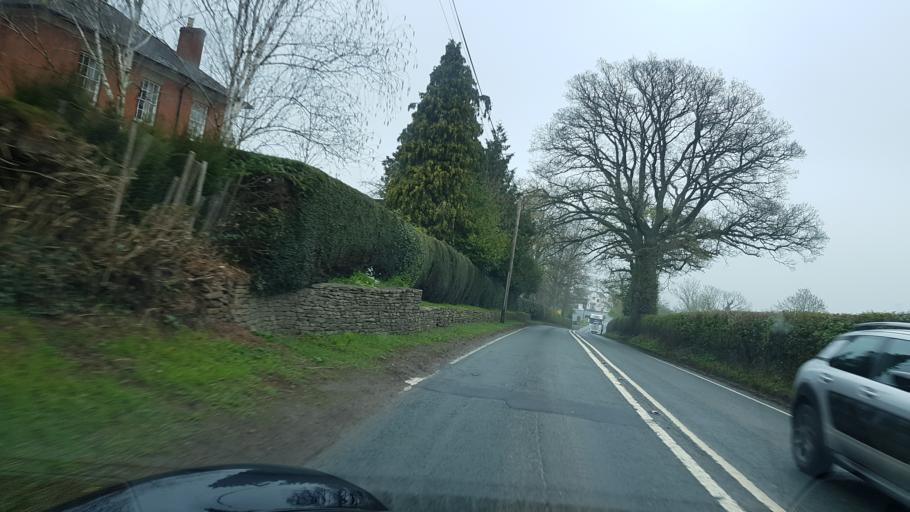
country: GB
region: England
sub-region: Herefordshire
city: Yatton
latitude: 52.0026
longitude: -2.4959
